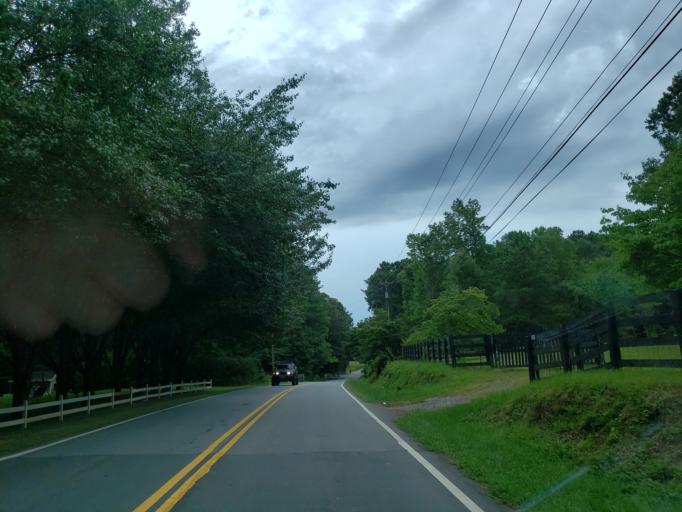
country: US
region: Georgia
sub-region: Cobb County
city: Acworth
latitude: 34.0247
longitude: -84.7261
